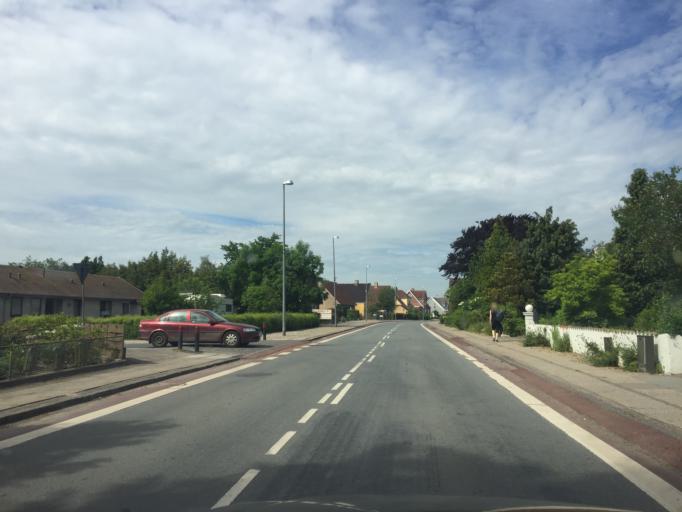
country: DK
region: South Denmark
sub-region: Faaborg-Midtfyn Kommune
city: Ringe
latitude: 55.2196
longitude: 10.6066
